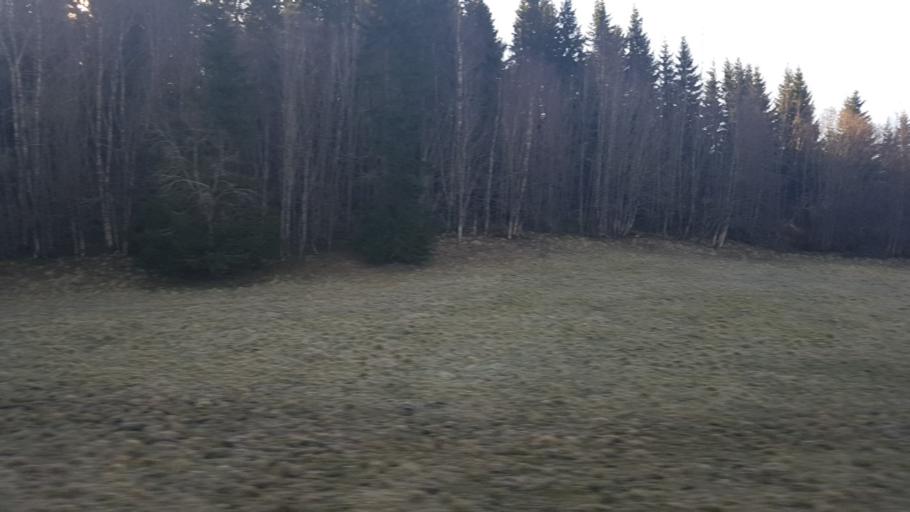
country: NO
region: Nord-Trondelag
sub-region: Levanger
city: Skogn
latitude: 63.6633
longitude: 11.1021
